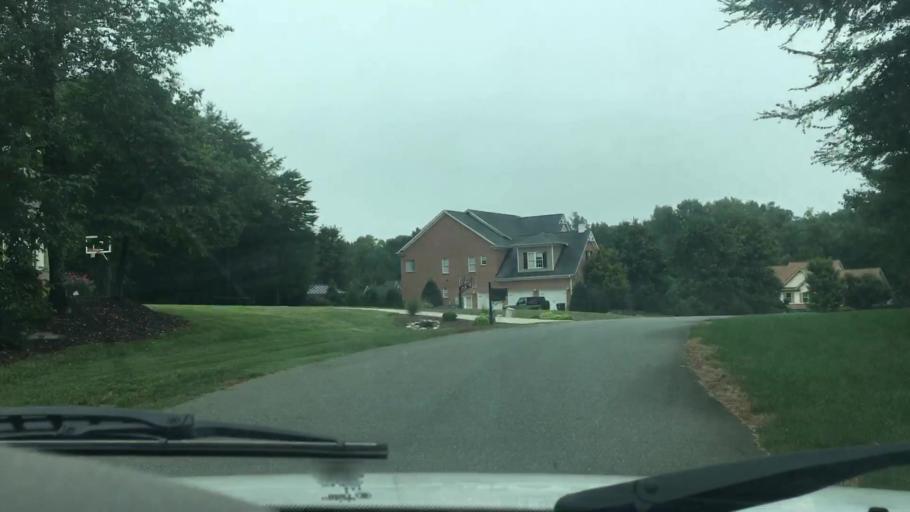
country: US
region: North Carolina
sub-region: Gaston County
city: Davidson
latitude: 35.5147
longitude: -80.7968
